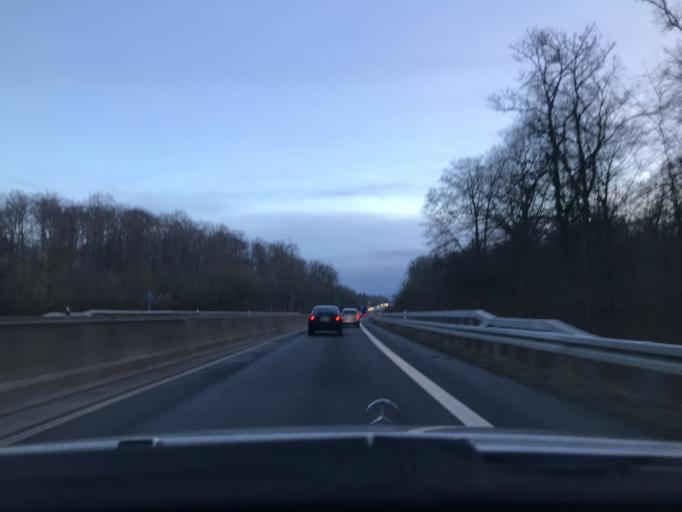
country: DE
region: Hesse
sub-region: Regierungsbezirk Kassel
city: Calden
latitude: 51.3915
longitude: 9.4332
